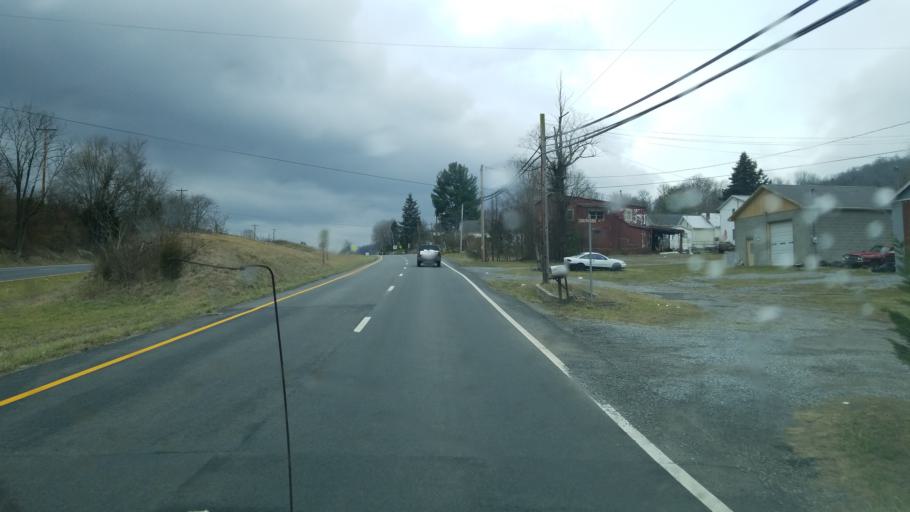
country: US
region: Virginia
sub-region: Giles County
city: Pearisburg
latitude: 37.3120
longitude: -80.7338
